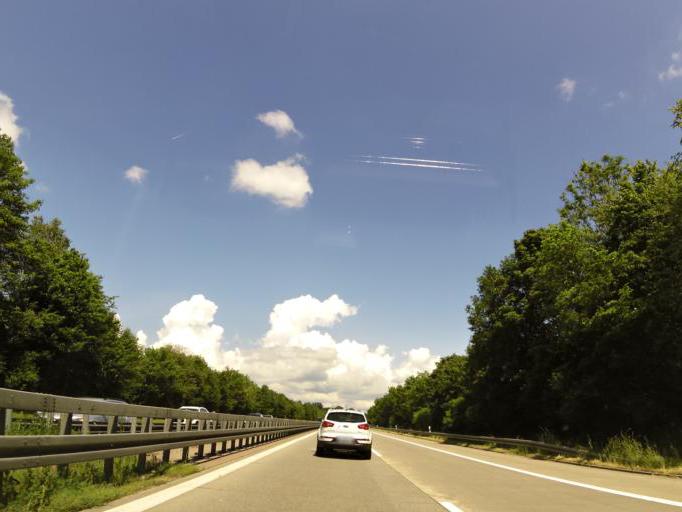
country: DE
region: Baden-Wuerttemberg
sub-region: Tuebingen Region
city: Nerenstetten
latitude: 48.5165
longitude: 10.0811
